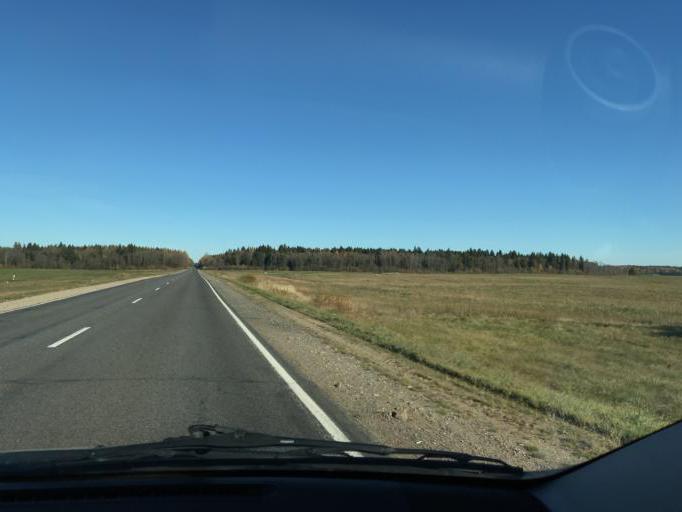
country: BY
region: Vitebsk
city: Lyepyel'
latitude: 54.9379
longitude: 28.7397
